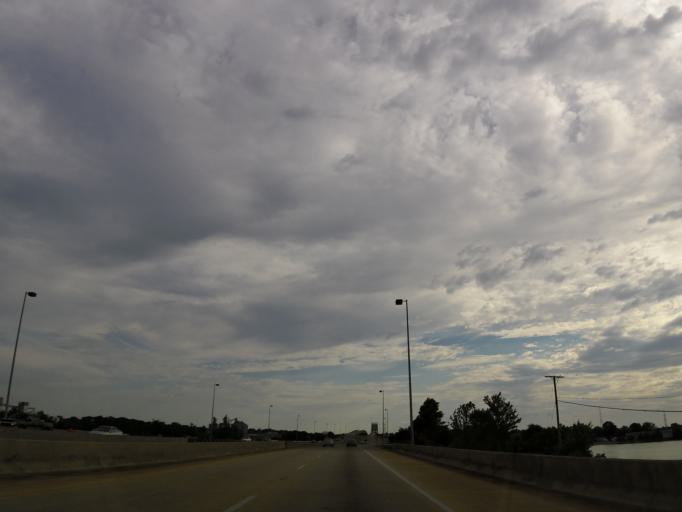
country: US
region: Alabama
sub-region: Morgan County
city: Decatur
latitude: 34.6198
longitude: -86.9658
